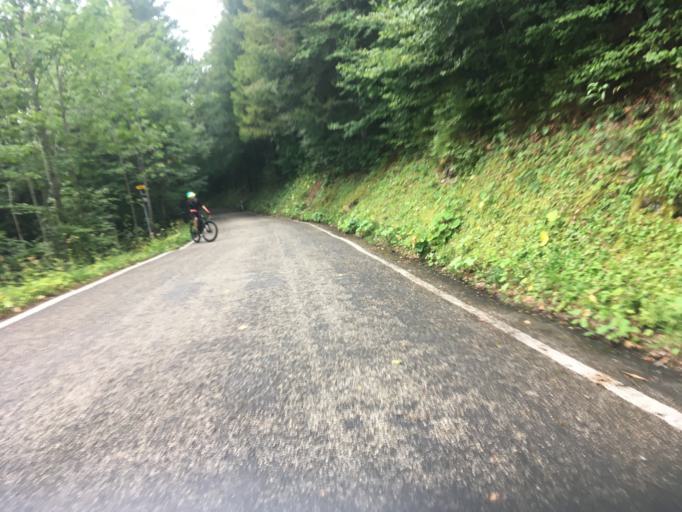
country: CH
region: Solothurn
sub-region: Bezirk Thal
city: Welschenrohr
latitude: 47.2549
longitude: 7.4976
